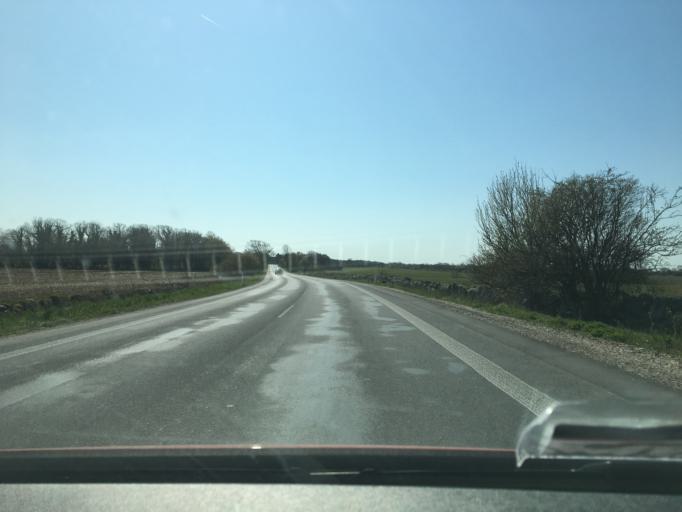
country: DK
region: Zealand
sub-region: Guldborgsund Kommune
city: Nykobing Falster
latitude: 54.7319
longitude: 11.7980
